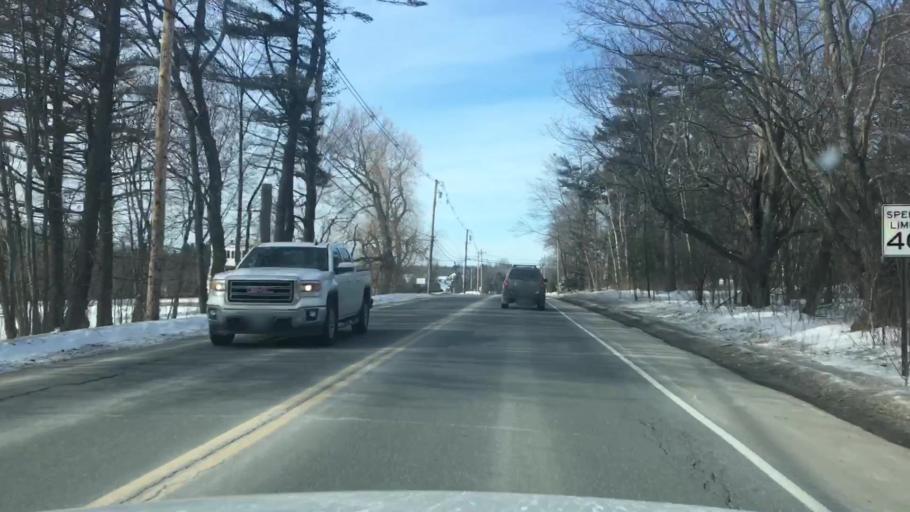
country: US
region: Maine
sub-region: Penobscot County
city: Bangor
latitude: 44.8478
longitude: -68.8026
